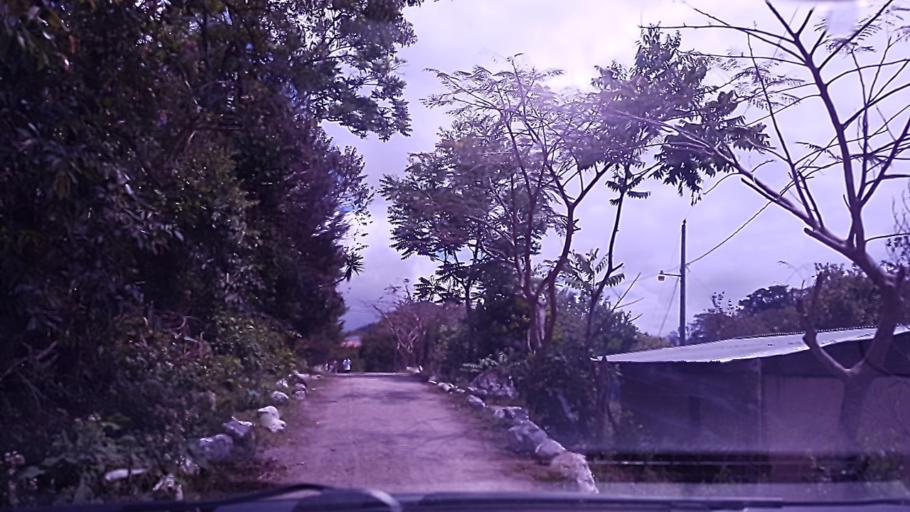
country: NI
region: Madriz
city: Telpaneca
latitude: 13.4249
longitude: -86.2585
